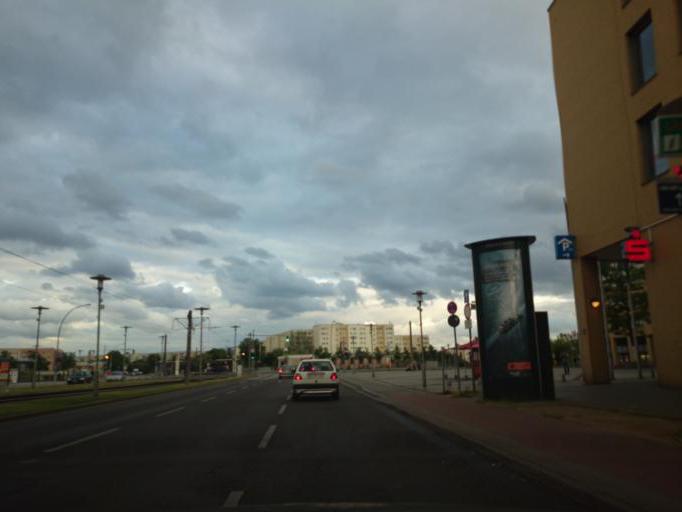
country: DE
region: Berlin
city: Hellersdorf
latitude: 52.5375
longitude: 13.6044
